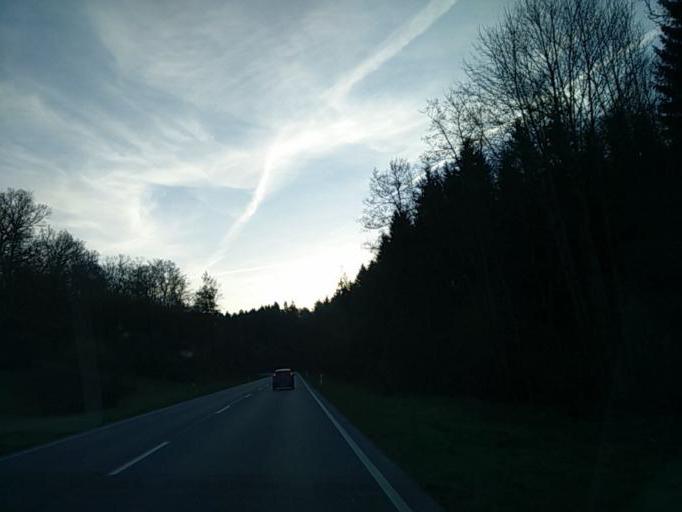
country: DE
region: Baden-Wuerttemberg
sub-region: Tuebingen Region
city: Tuebingen
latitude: 48.5664
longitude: 9.0704
